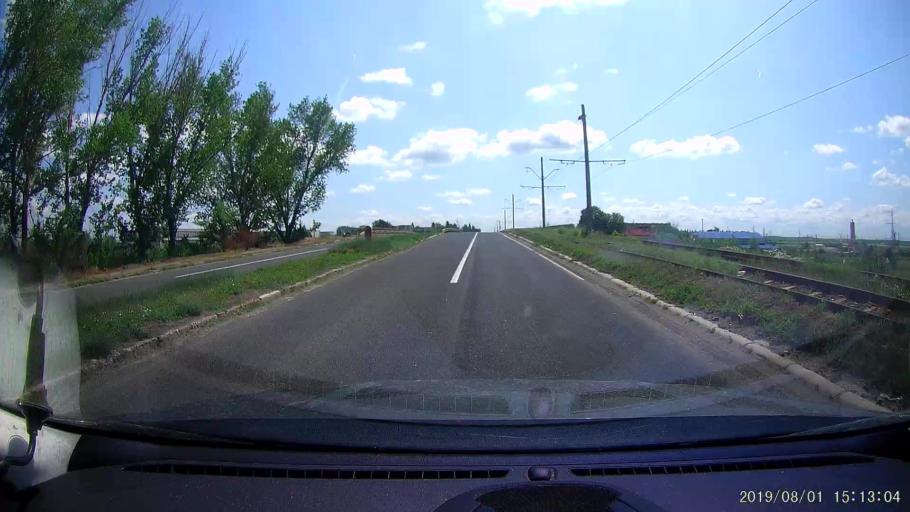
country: RO
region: Braila
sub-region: Comuna Chiscani
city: Lacu Sarat
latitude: 45.1974
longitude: 27.9039
